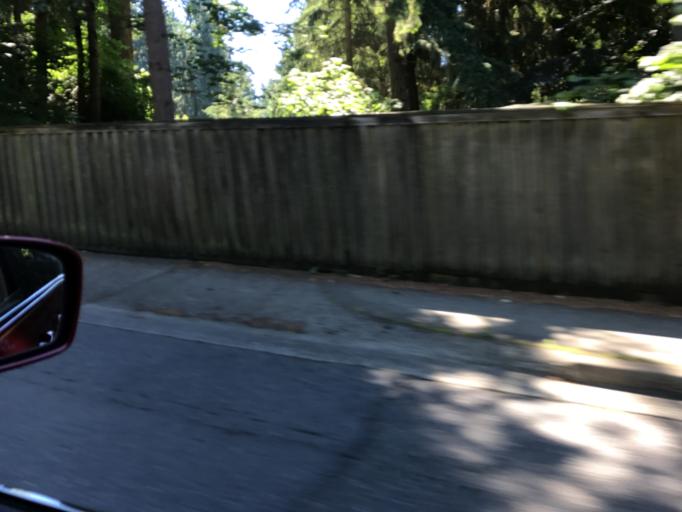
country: US
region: Washington
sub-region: King County
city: Eastgate
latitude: 47.6253
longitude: -122.1489
